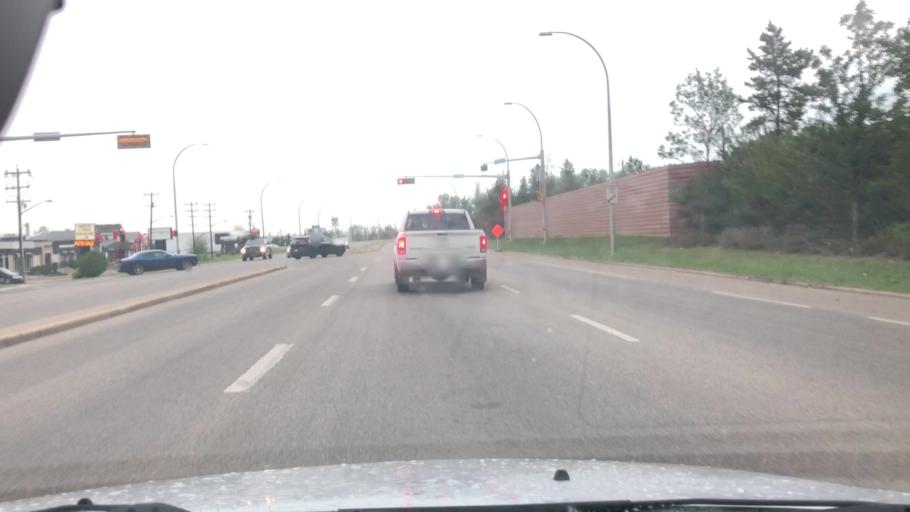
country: CA
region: Alberta
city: St. Albert
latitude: 53.5555
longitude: -113.6055
